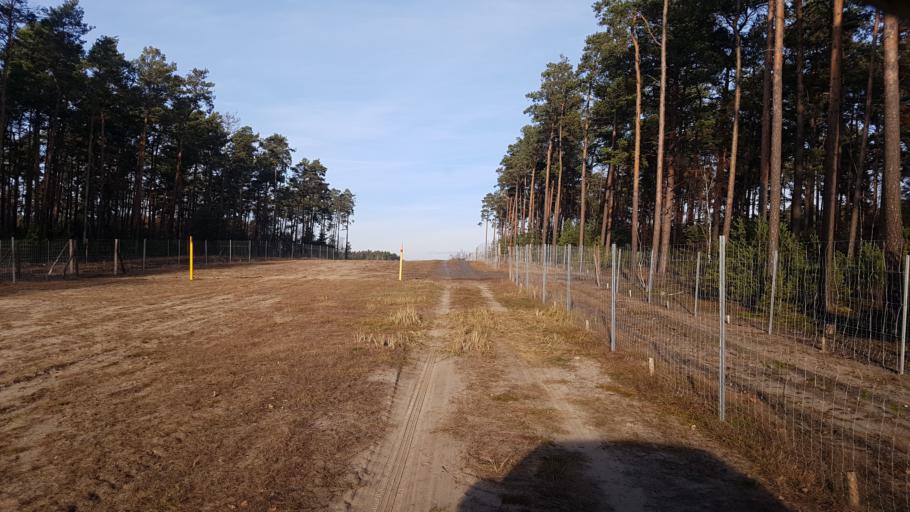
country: DE
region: Brandenburg
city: Finsterwalde
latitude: 51.6303
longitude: 13.6659
